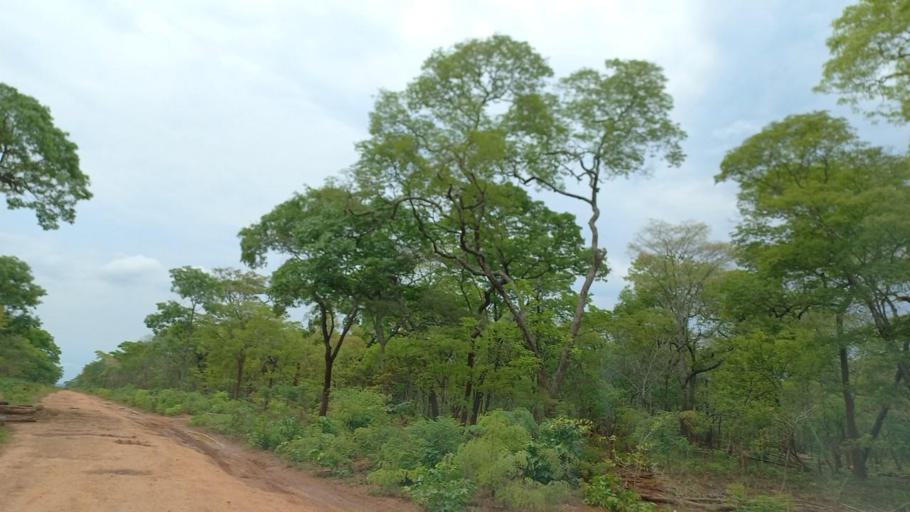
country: ZM
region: North-Western
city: Kalengwa
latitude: -13.6121
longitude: 24.9756
